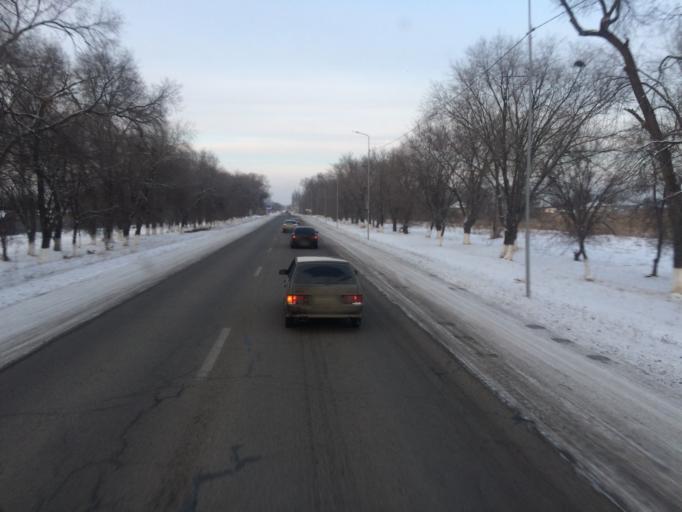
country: KZ
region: Almaty Oblysy
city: Burunday
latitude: 43.2640
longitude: 76.6699
